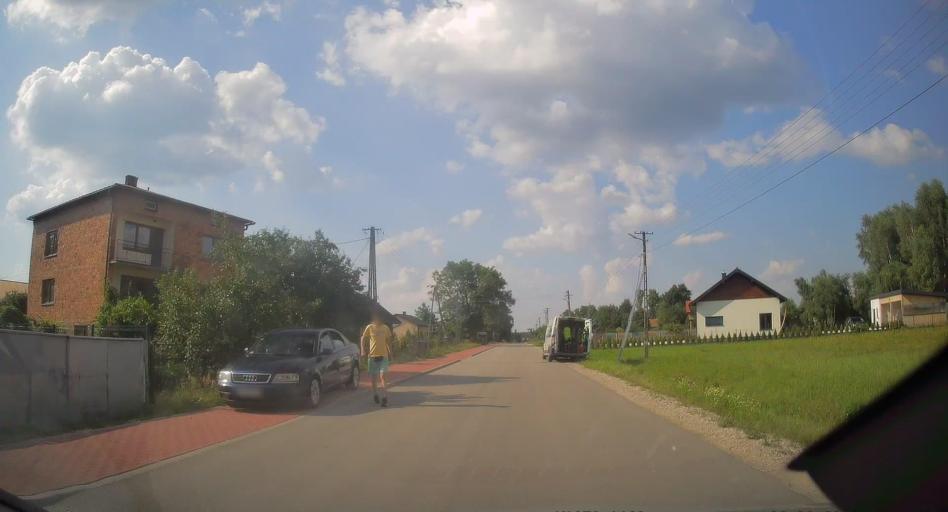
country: PL
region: Swietokrzyskie
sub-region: Powiat konecki
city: Radoszyce
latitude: 51.1122
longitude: 20.2628
